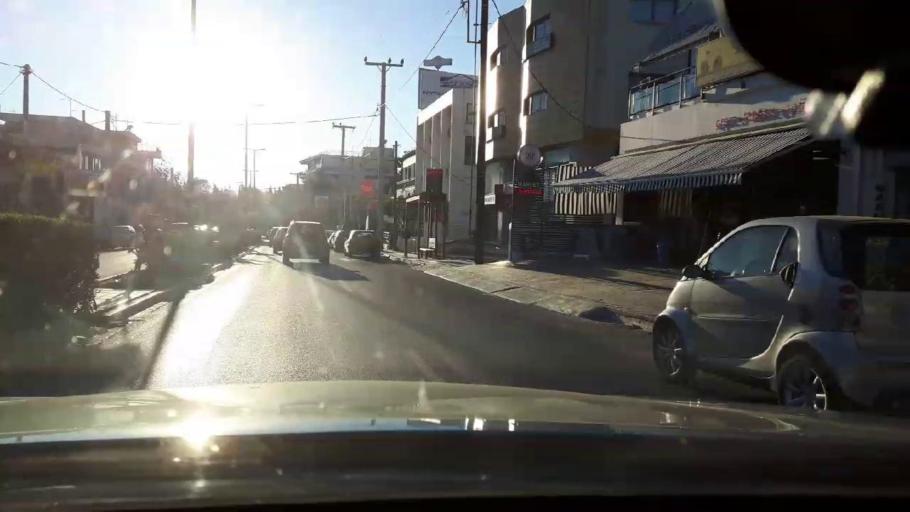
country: GR
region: Attica
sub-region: Nomarchia Athinas
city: Melissia
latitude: 38.0524
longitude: 23.8283
